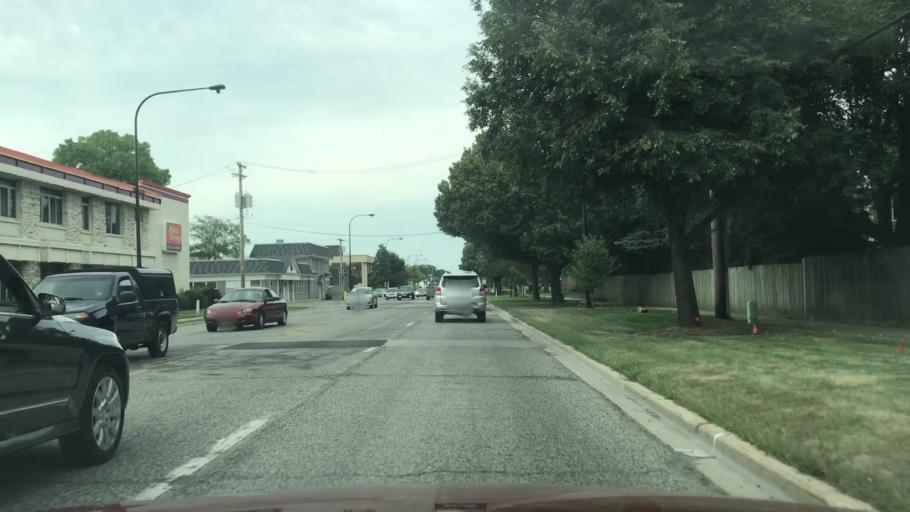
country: US
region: Illinois
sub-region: Cook County
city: Mount Prospect
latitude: 42.0663
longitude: -87.9483
